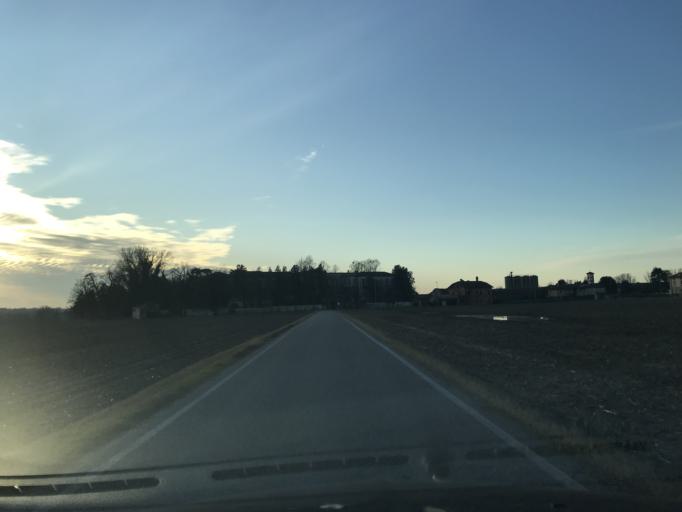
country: IT
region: Lombardy
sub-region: Provincia di Lodi
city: Graffignana
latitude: 45.2135
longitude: 9.4693
